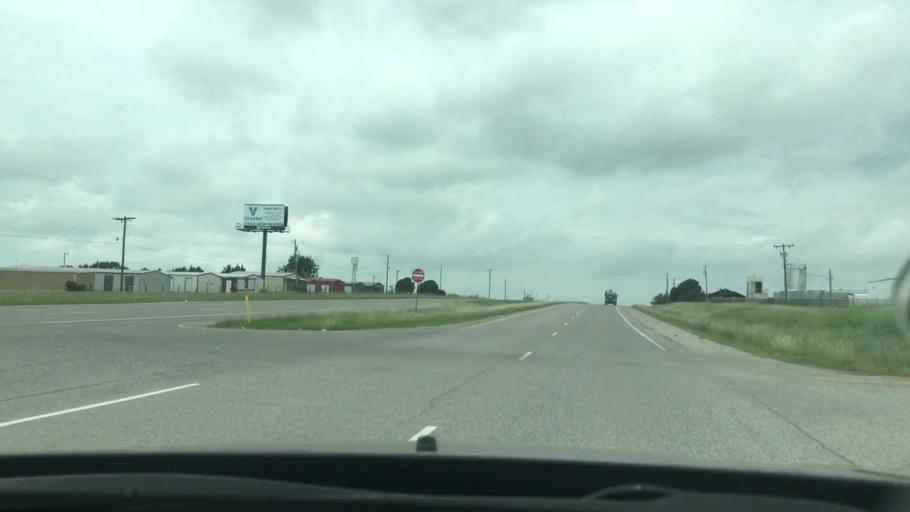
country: US
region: Oklahoma
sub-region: Carter County
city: Wilson
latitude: 34.1732
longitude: -97.4393
